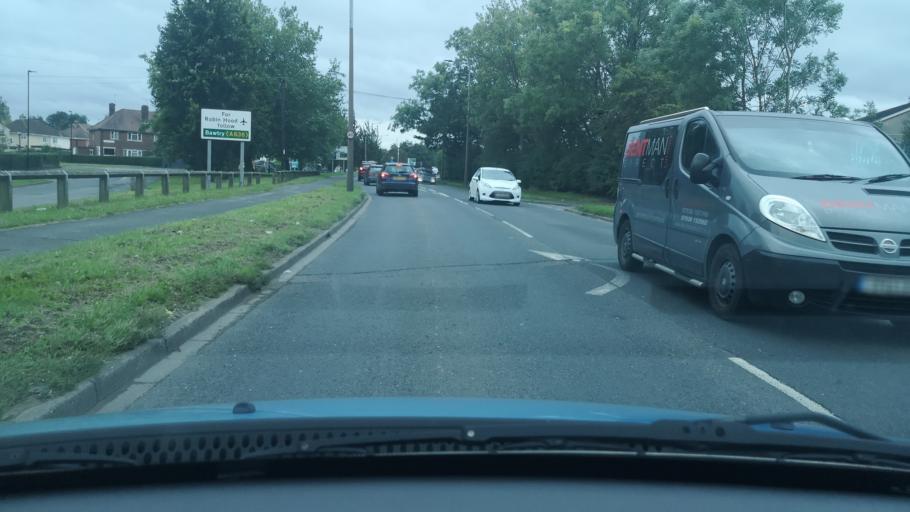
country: GB
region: England
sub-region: Doncaster
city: Kirk Sandall
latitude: 53.5504
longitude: -1.0861
